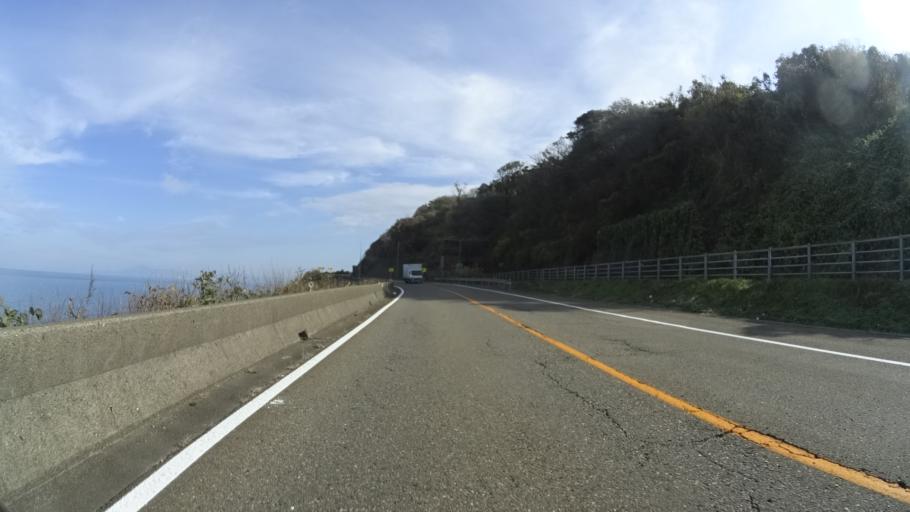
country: JP
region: Niigata
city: Joetsu
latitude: 37.1708
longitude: 138.1158
